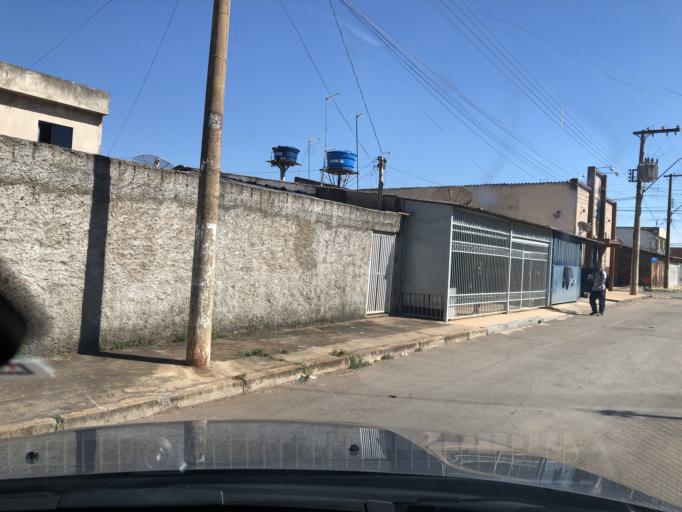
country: BR
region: Federal District
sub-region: Brasilia
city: Brasilia
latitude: -15.8064
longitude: -48.1412
